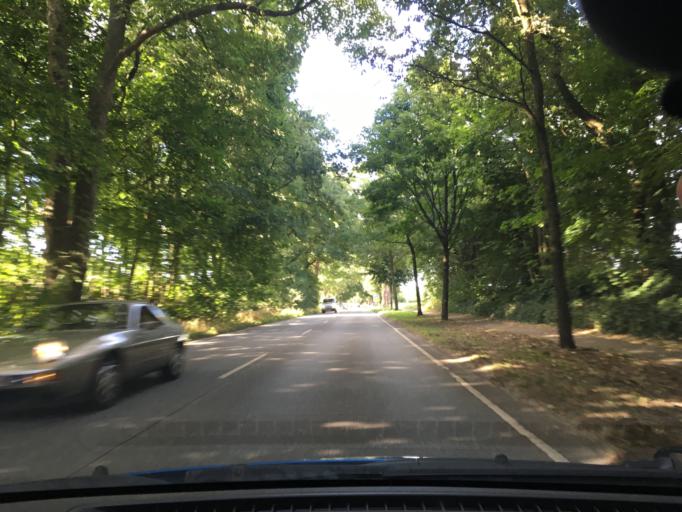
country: DE
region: Lower Saxony
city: Seevetal
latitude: 53.4261
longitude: 9.9310
